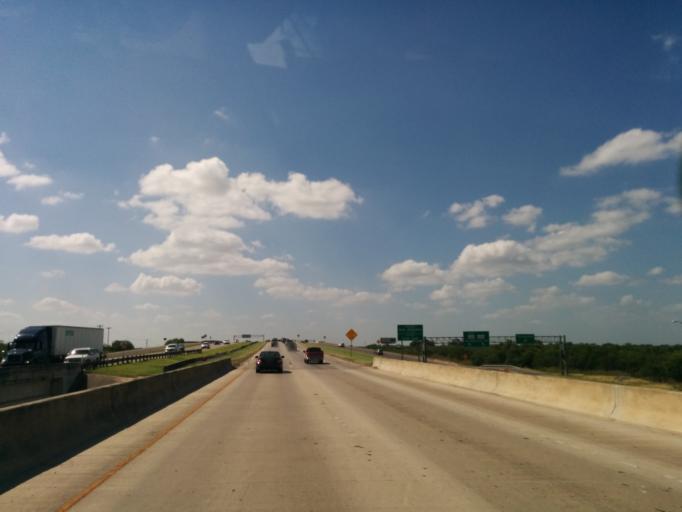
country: US
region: Texas
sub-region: Bexar County
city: Live Oak
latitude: 29.5786
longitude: -98.3427
